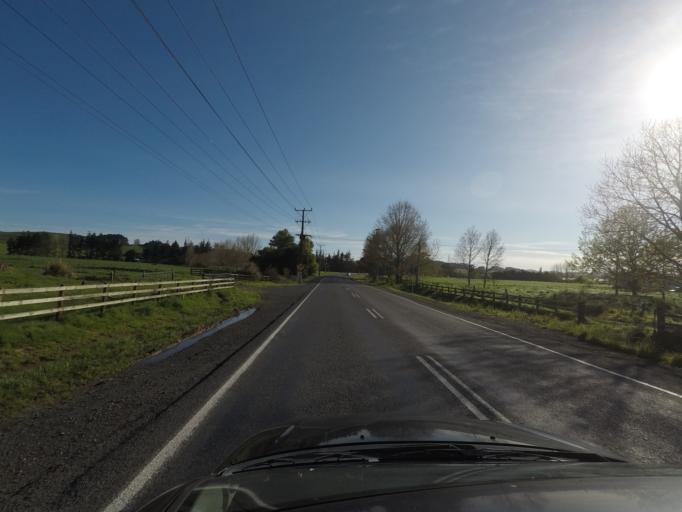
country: NZ
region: Auckland
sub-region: Auckland
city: Red Hill
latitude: -37.0042
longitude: 174.9562
